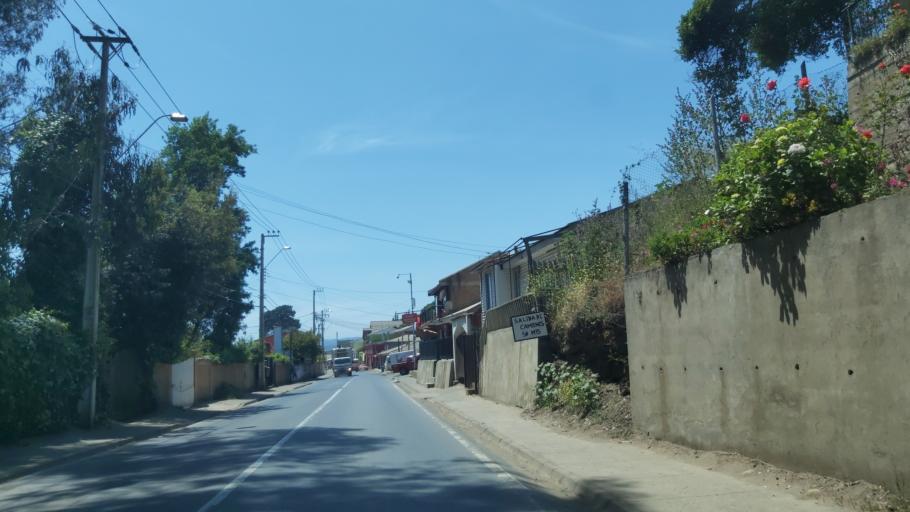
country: CL
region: Maule
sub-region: Provincia de Cauquenes
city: Cauquenes
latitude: -35.8172
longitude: -72.5863
